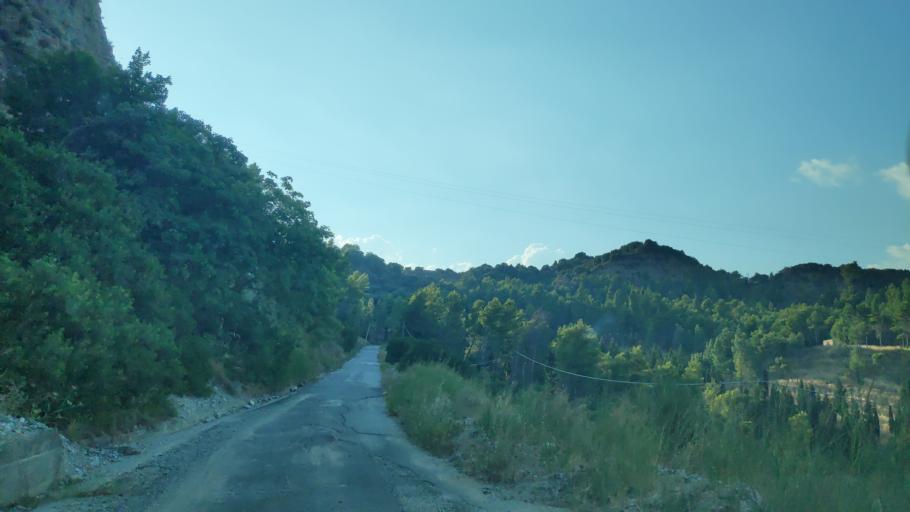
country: IT
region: Calabria
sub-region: Provincia di Reggio Calabria
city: Placanica
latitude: 38.4096
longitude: 16.4326
